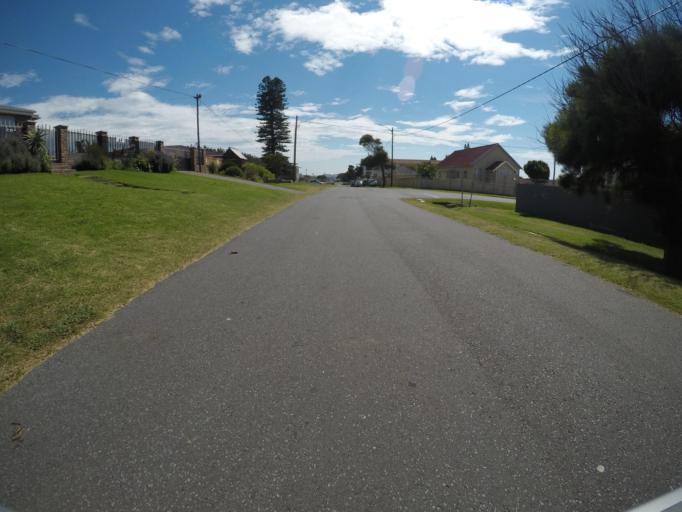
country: ZA
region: Eastern Cape
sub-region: Buffalo City Metropolitan Municipality
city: East London
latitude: -33.0356
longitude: 27.9040
